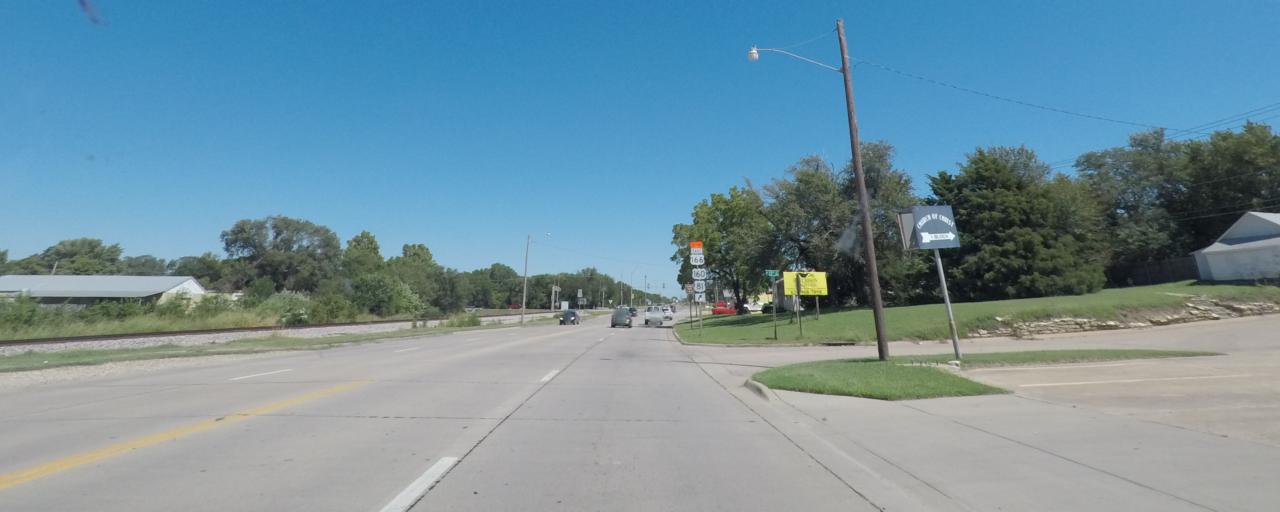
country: US
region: Kansas
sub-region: Sumner County
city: Wellington
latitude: 37.2724
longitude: -97.4020
